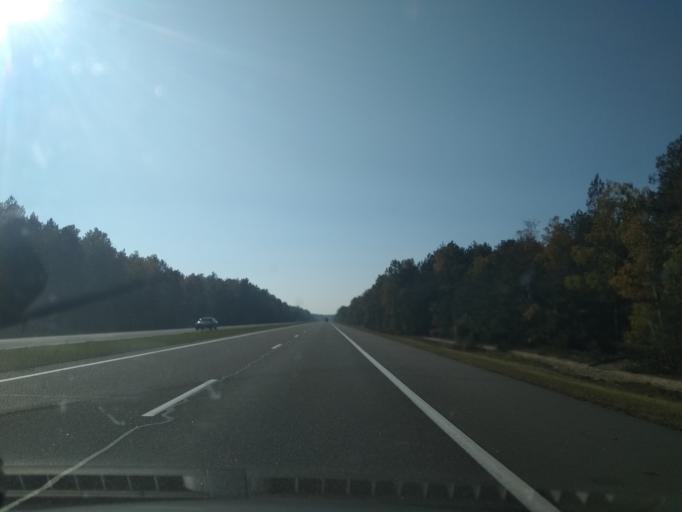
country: BY
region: Brest
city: Antopal'
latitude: 52.3782
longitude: 24.7556
